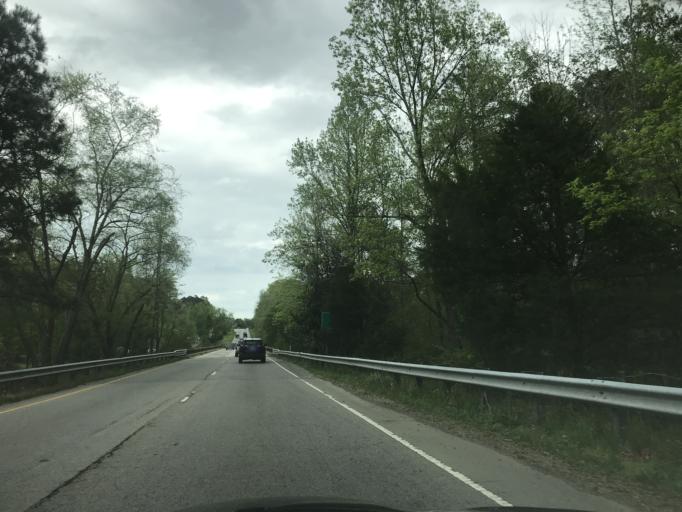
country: US
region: North Carolina
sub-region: Wake County
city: Knightdale
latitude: 35.7928
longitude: -78.5401
